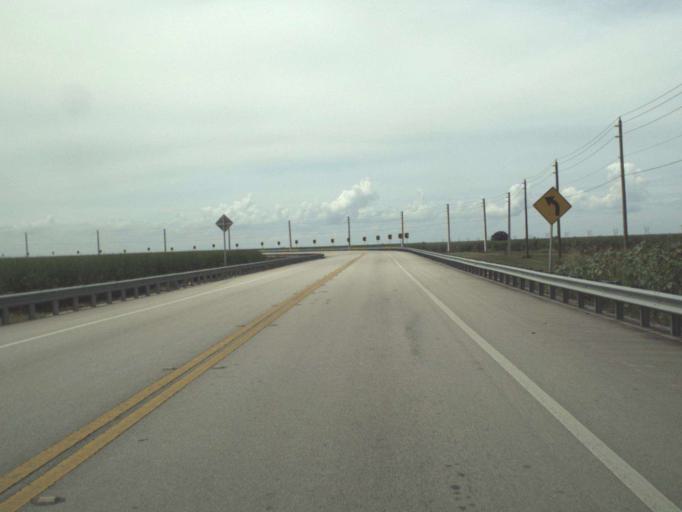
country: US
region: Florida
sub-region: Palm Beach County
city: Pahokee
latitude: 26.7695
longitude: -80.6560
